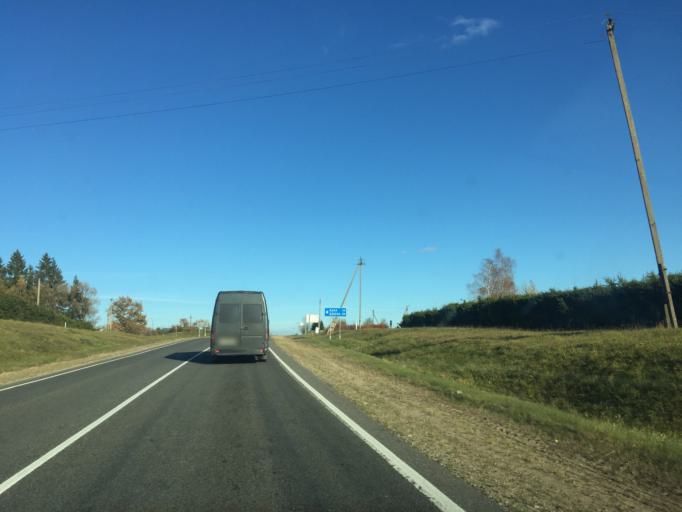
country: BY
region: Vitebsk
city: Dzisna
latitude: 55.2987
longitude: 28.2115
